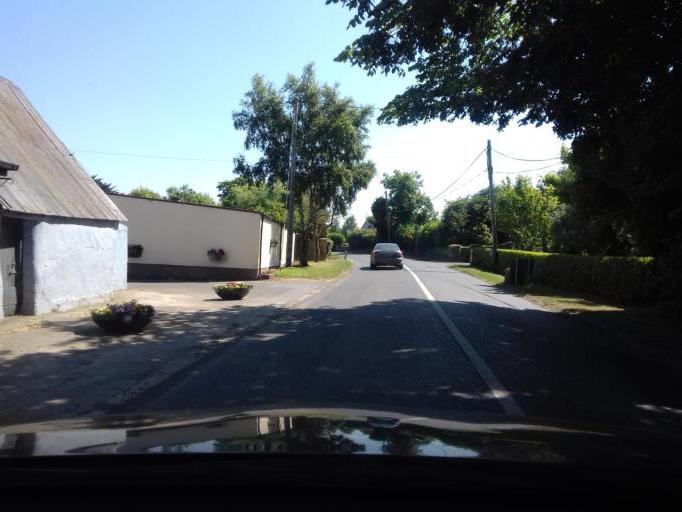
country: IE
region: Leinster
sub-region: An Mhi
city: Stamullin
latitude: 53.5762
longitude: -6.2839
